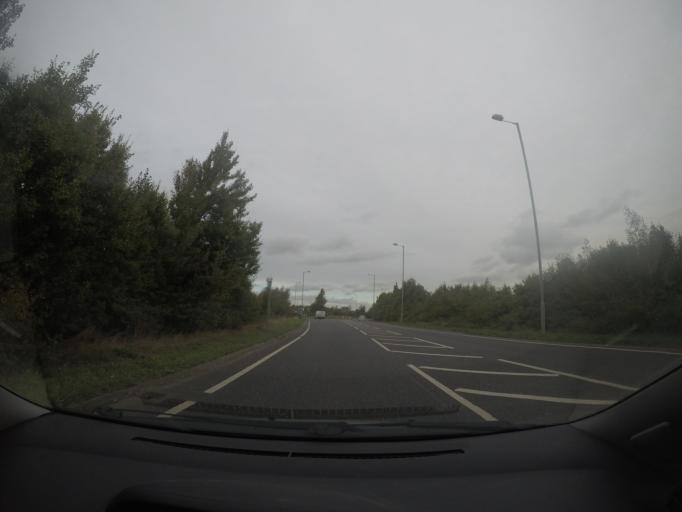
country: GB
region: England
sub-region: North Yorkshire
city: Barlby
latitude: 53.7811
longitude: -1.0361
